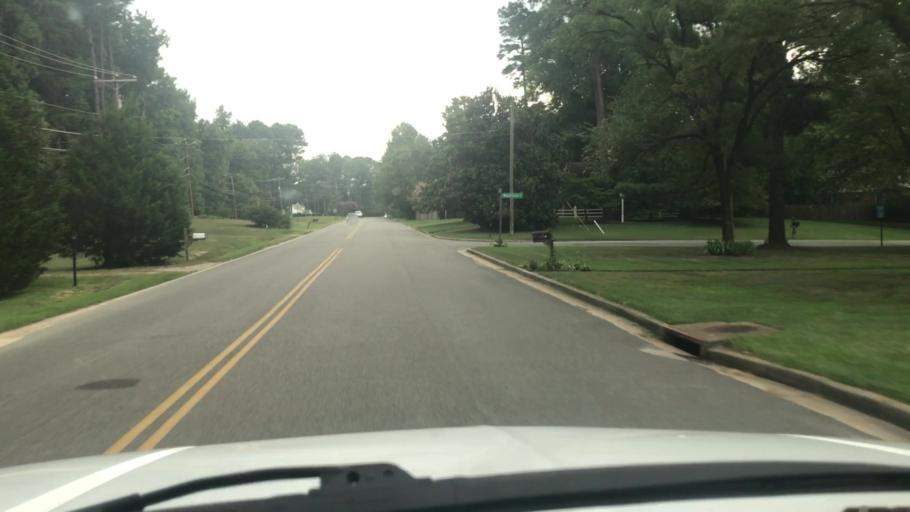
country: US
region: Virginia
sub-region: Henrico County
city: Tuckahoe
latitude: 37.6018
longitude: -77.5852
